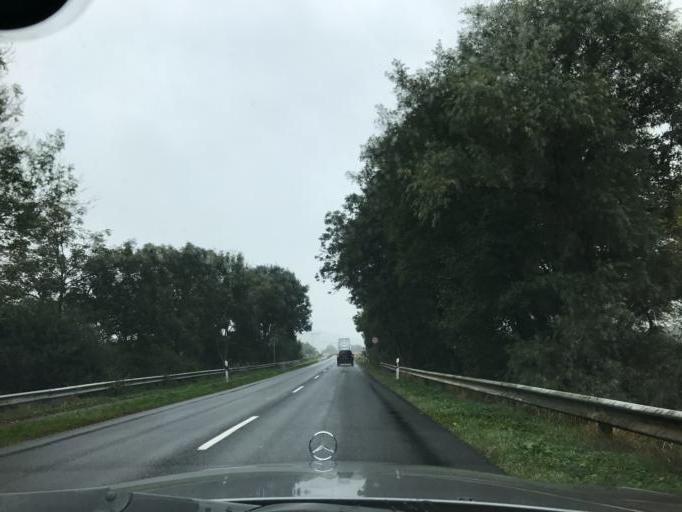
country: DE
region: Lower Saxony
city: Weener
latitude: 53.1073
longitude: 7.3500
